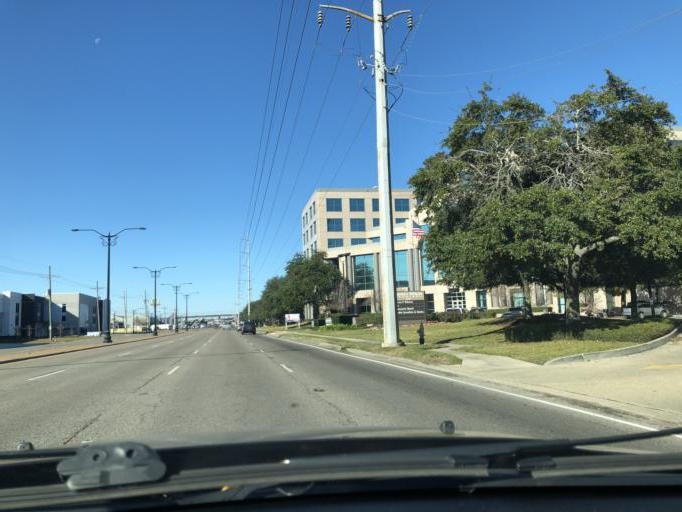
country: US
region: Louisiana
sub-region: Jefferson Parish
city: Jefferson
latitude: 29.9740
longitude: -90.1478
